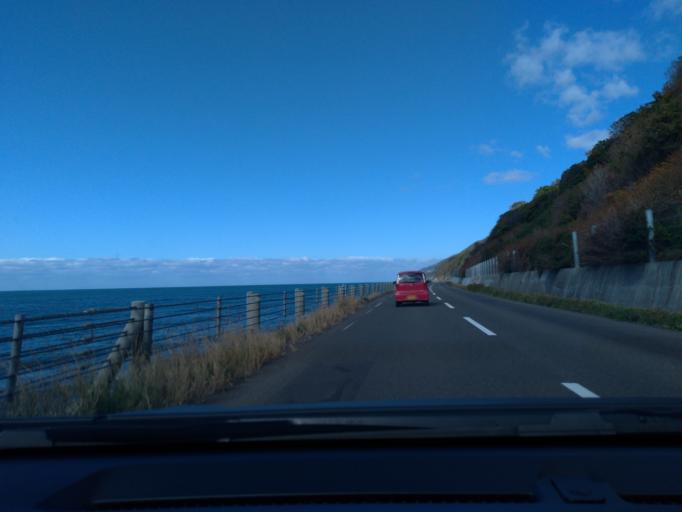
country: JP
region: Hokkaido
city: Ishikari
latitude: 43.4273
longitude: 141.4231
